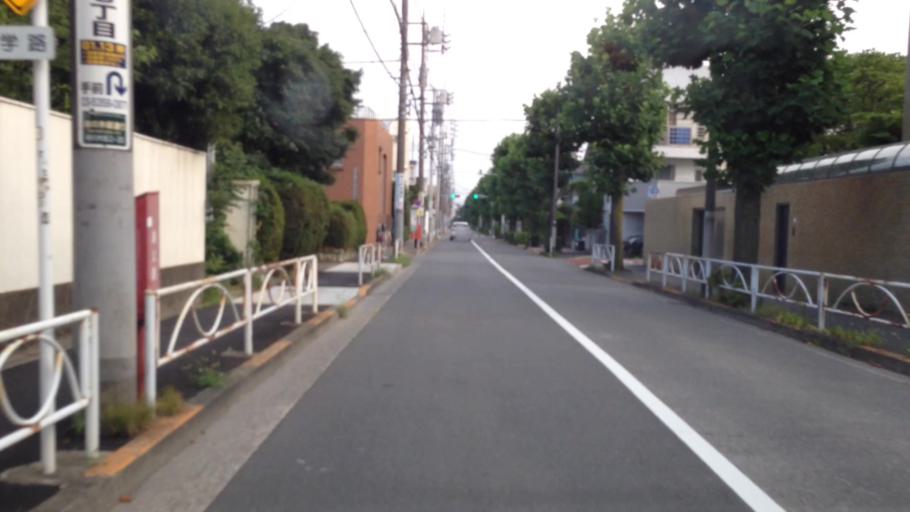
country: JP
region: Tokyo
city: Tokyo
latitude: 35.6260
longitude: 139.6724
